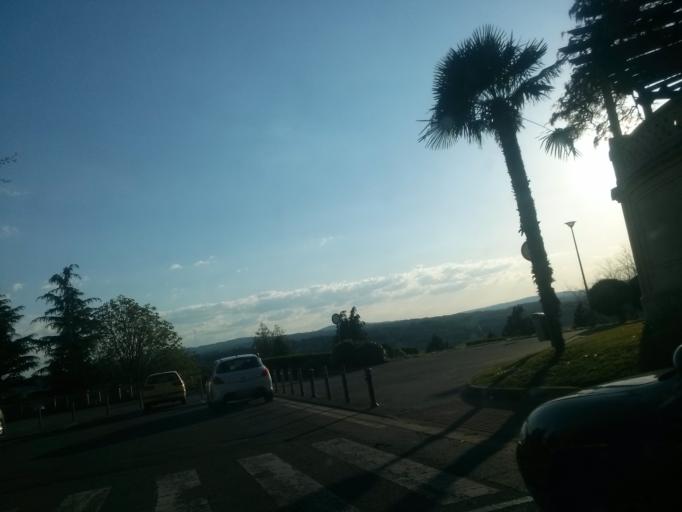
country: ES
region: Galicia
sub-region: Provincia de Lugo
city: Lugo
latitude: 43.0047
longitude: -7.5596
